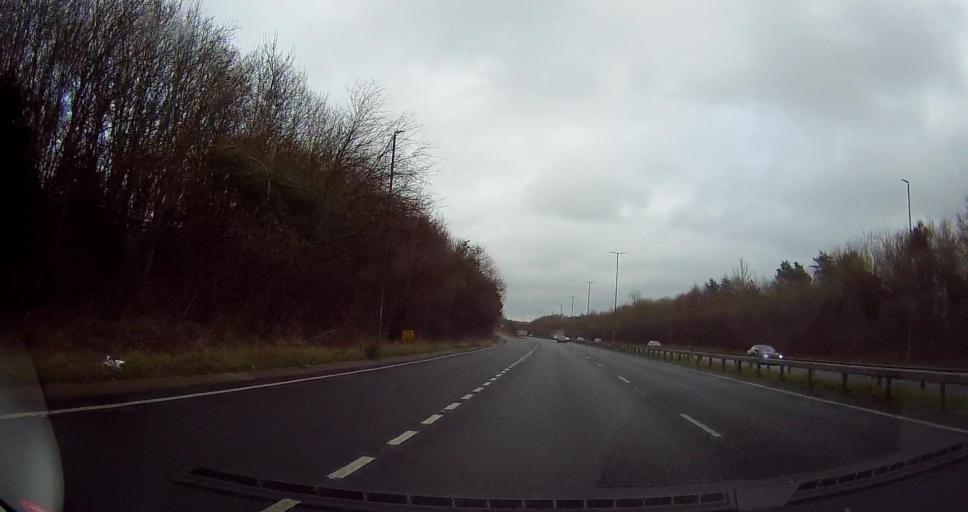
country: GB
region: England
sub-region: Medway
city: Cuxton
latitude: 51.4061
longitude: 0.4597
